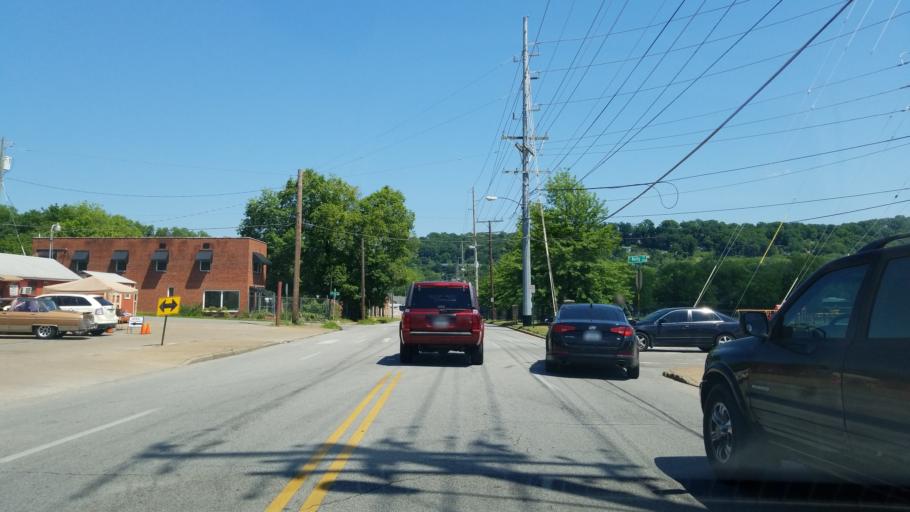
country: US
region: Tennessee
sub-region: Hamilton County
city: East Ridge
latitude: 35.0247
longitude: -85.2763
